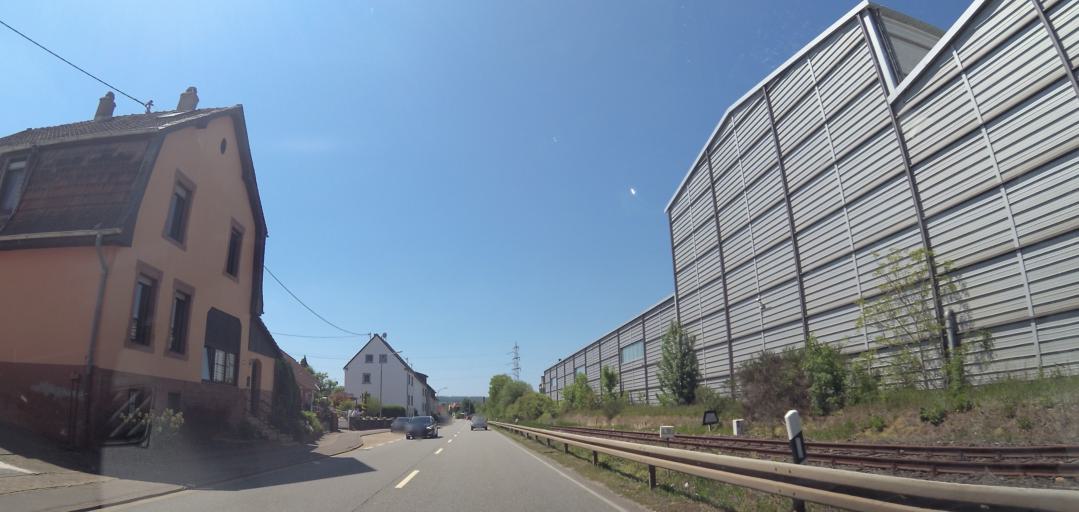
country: DE
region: Saarland
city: Merzig
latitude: 49.4495
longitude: 6.6590
